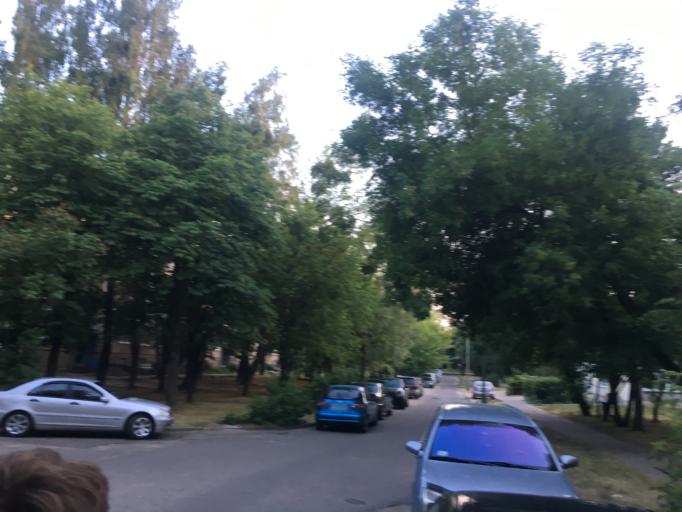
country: BY
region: Grodnenskaya
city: Hrodna
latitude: 53.7071
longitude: 23.7979
